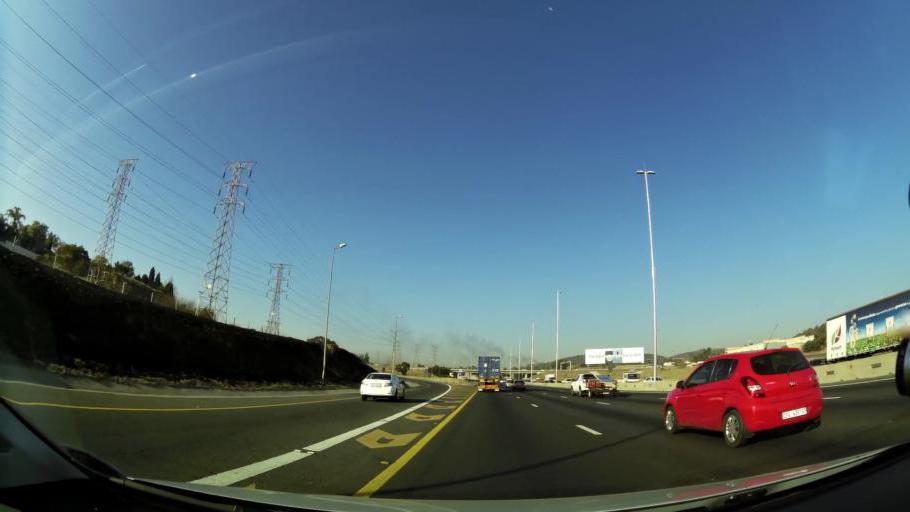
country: ZA
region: Gauteng
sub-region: City of Johannesburg Metropolitan Municipality
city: Modderfontein
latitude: -26.1459
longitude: 28.1316
